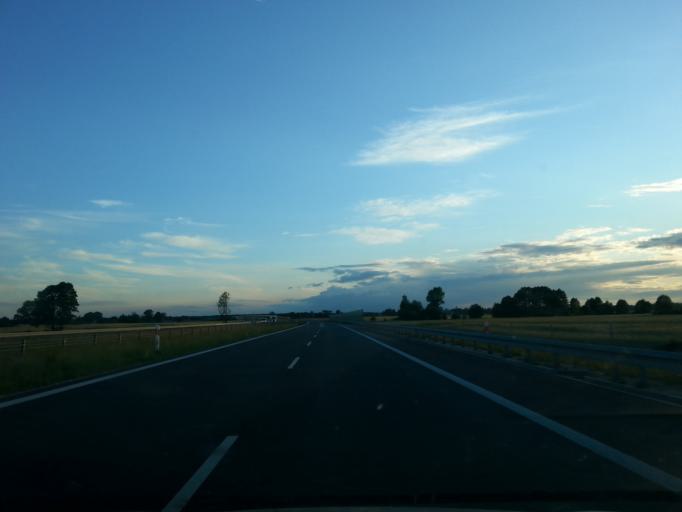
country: PL
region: Greater Poland Voivodeship
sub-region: Powiat kepinski
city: Bralin
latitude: 51.3111
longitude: 17.9366
